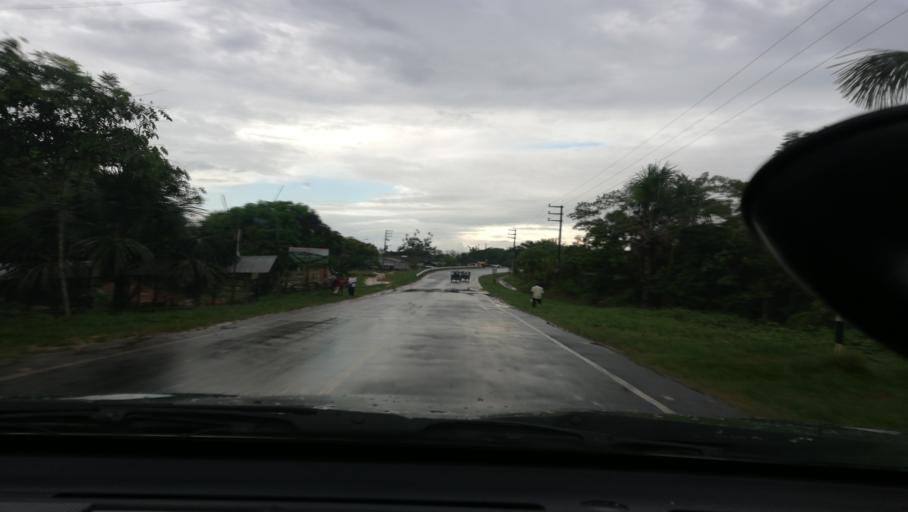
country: PE
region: Loreto
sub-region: Provincia de Maynas
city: Iquitos
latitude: -3.8937
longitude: -73.3490
